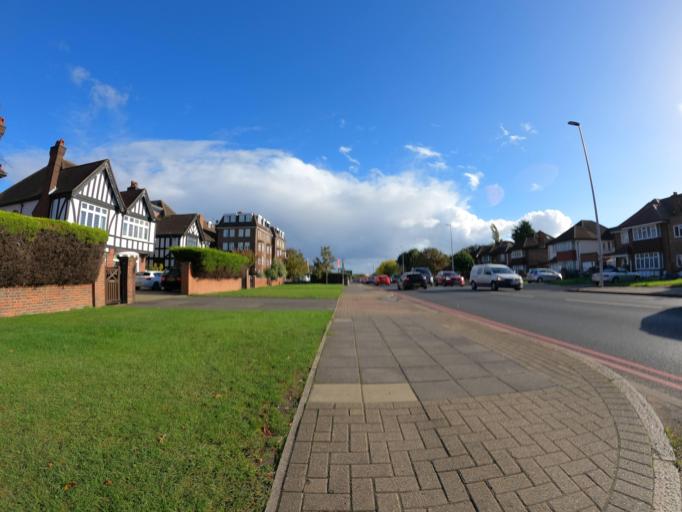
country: GB
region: England
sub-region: Greater London
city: Acton
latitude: 51.5026
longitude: -0.2876
